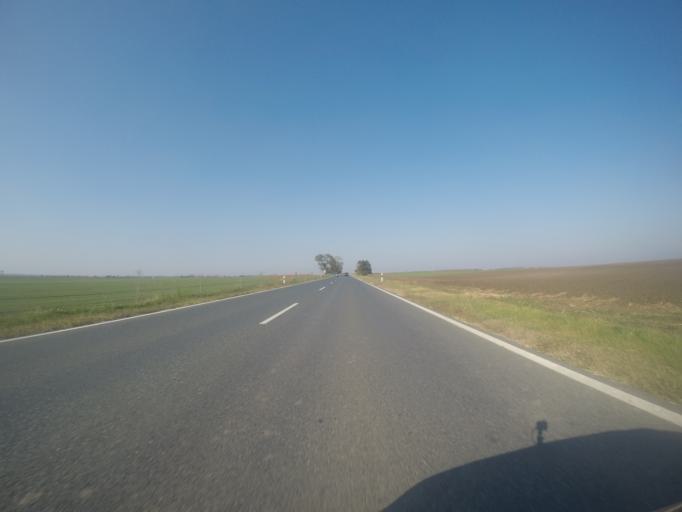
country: HU
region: Tolna
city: Madocsa
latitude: 46.7138
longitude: 18.8869
